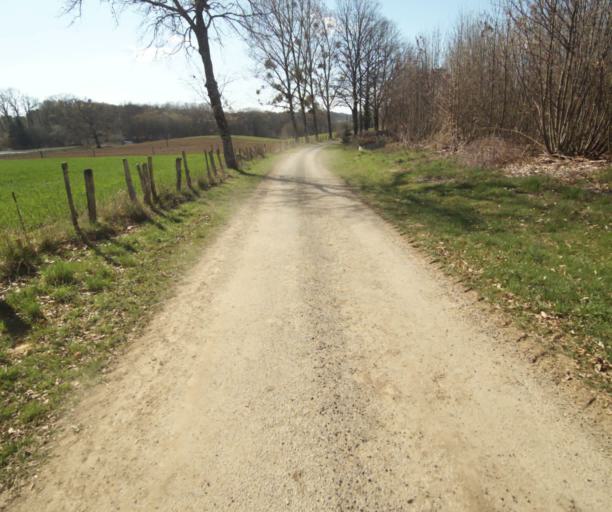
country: FR
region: Limousin
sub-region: Departement de la Correze
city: Saint-Mexant
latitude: 45.2864
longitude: 1.6858
